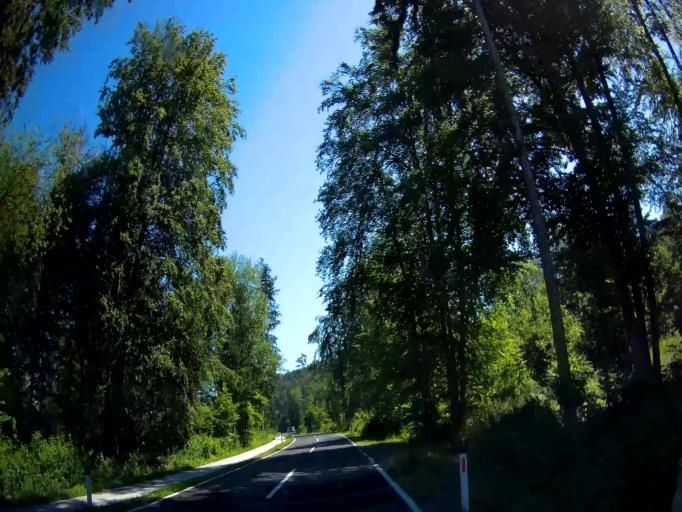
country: AT
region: Carinthia
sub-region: Politischer Bezirk Volkermarkt
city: Sittersdorf
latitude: 46.5570
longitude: 14.6191
